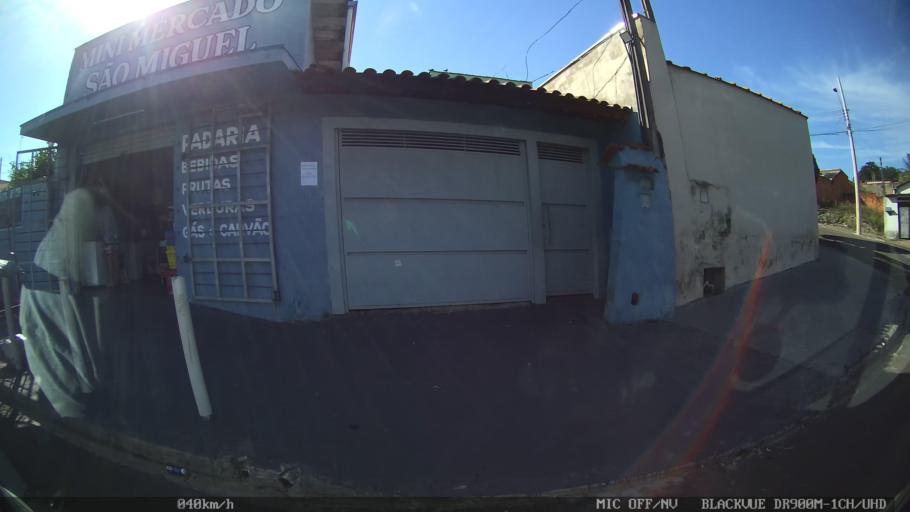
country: BR
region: Sao Paulo
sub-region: Franca
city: Franca
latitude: -20.4912
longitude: -47.4208
